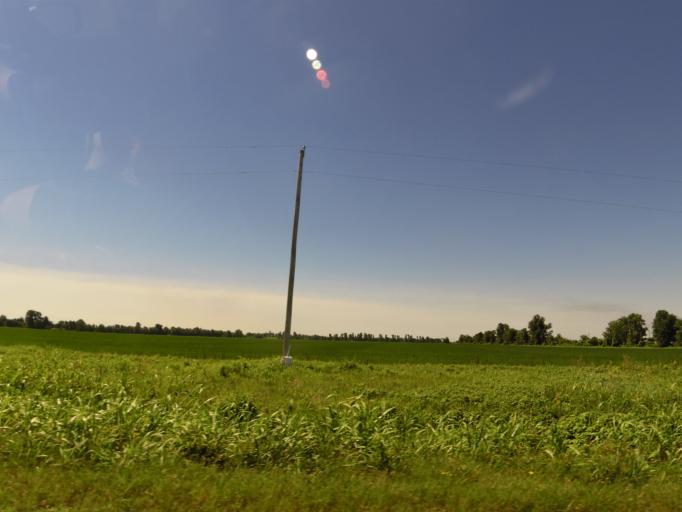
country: US
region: Missouri
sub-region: New Madrid County
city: Lilbourn
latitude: 36.5549
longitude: -89.6817
